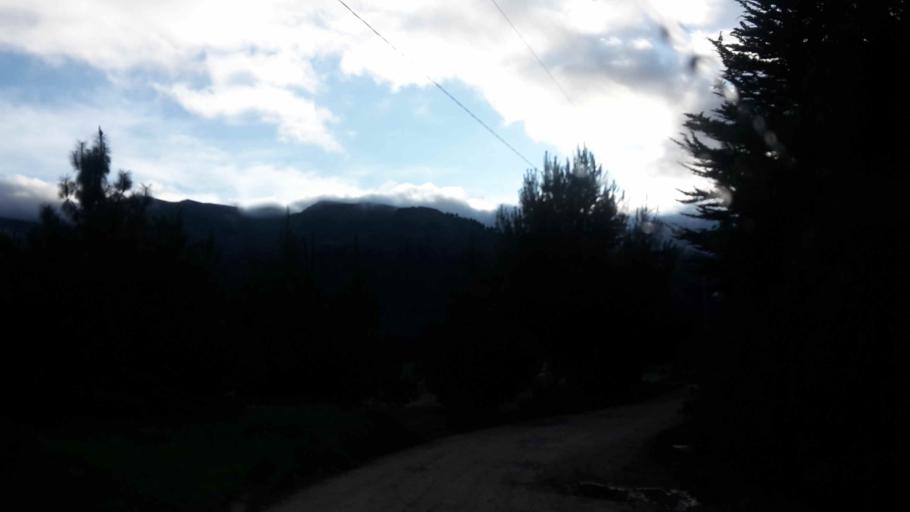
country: BO
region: Cochabamba
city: Colomi
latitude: -17.2785
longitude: -65.9107
